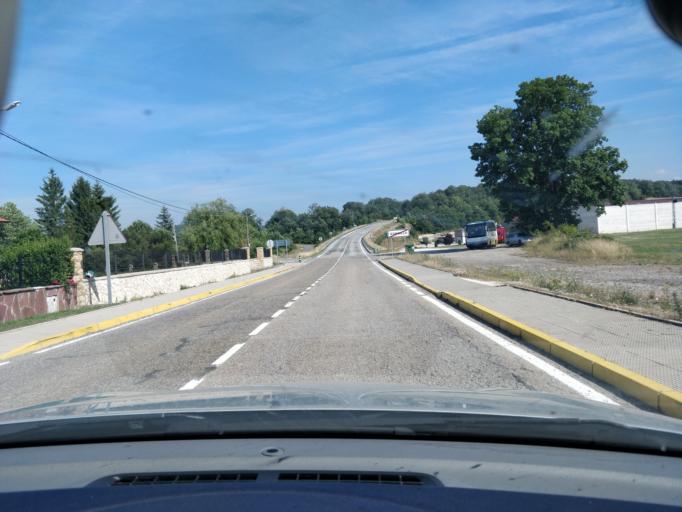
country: ES
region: Cantabria
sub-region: Provincia de Cantabria
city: San Pedro del Romeral
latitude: 42.9670
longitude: -3.7820
